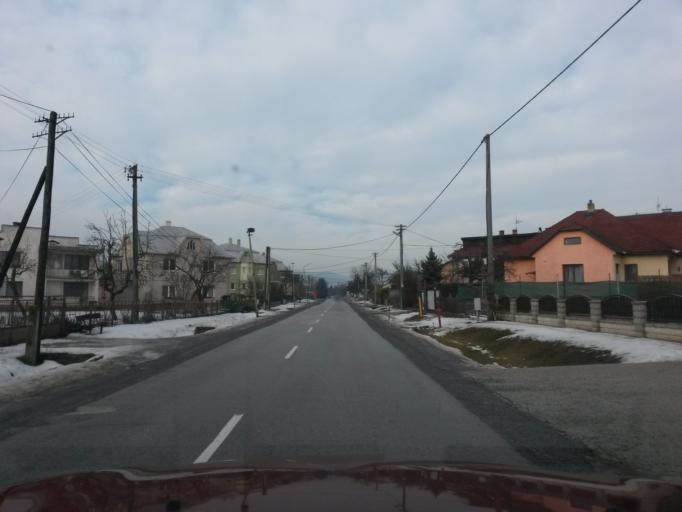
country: SK
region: Kosicky
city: Kosice
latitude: 48.7811
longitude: 21.3281
